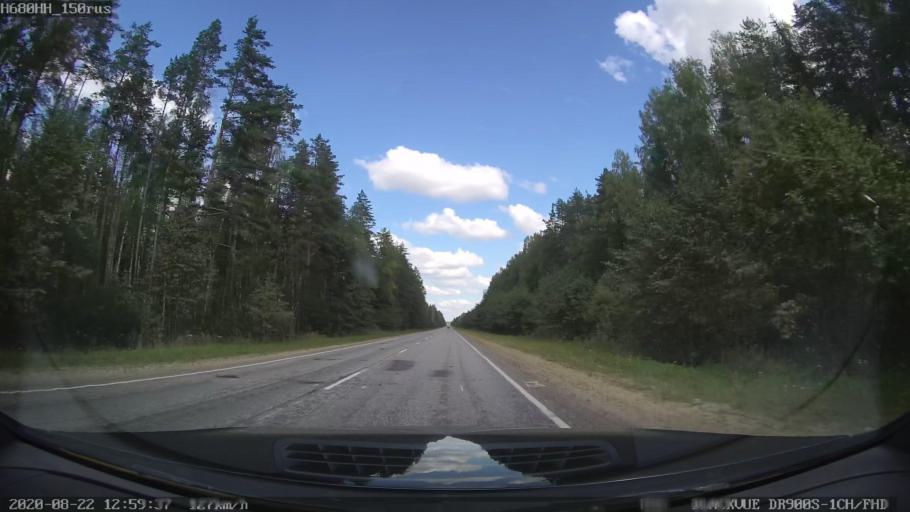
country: RU
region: Tverskaya
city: Bezhetsk
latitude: 57.6091
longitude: 36.3626
